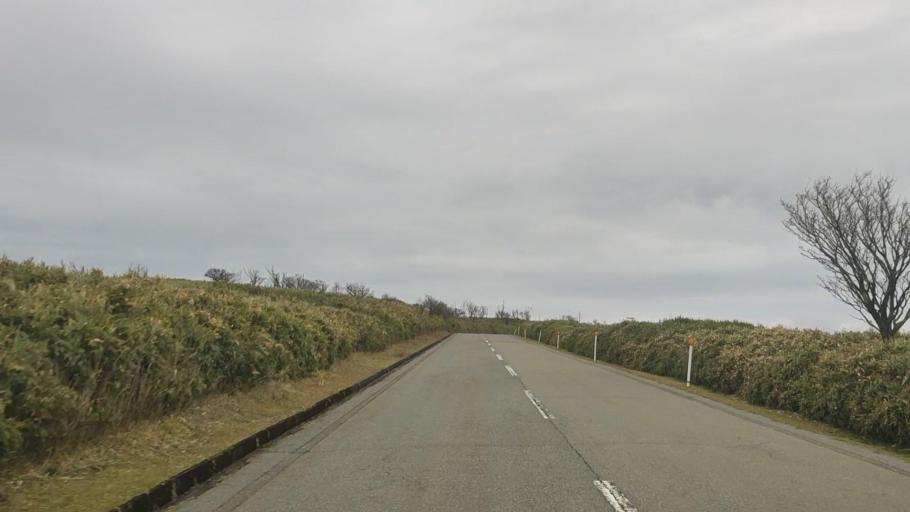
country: JP
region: Shizuoka
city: Heda
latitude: 34.9414
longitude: 138.8374
